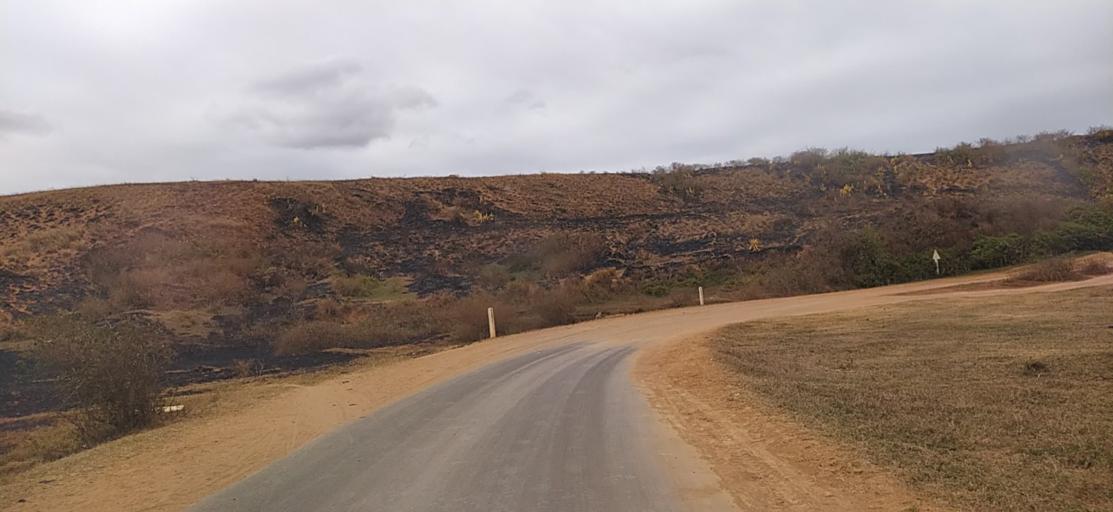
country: MG
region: Alaotra Mangoro
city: Ambatondrazaka
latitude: -17.9121
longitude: 48.2616
